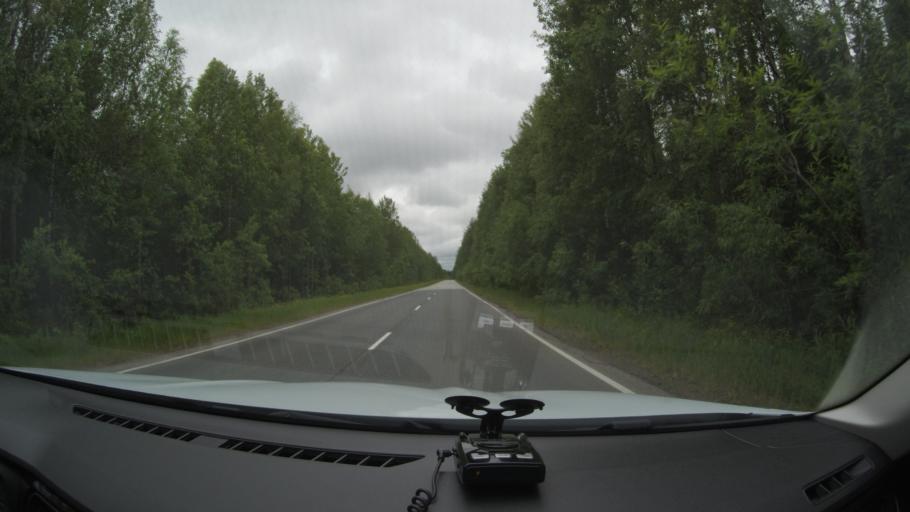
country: RU
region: Komi Republic
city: Nizhniy Odes
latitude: 63.6227
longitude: 54.6148
